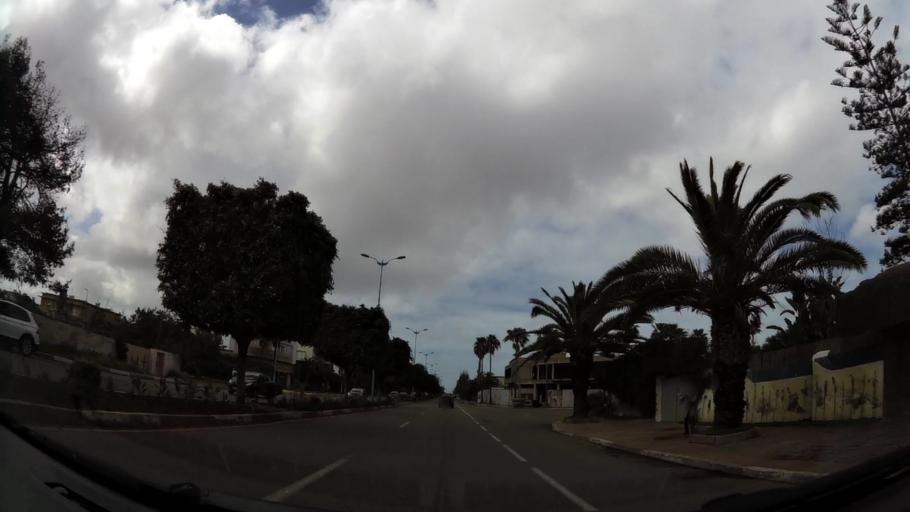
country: MA
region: Grand Casablanca
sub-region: Casablanca
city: Casablanca
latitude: 33.5428
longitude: -7.6309
